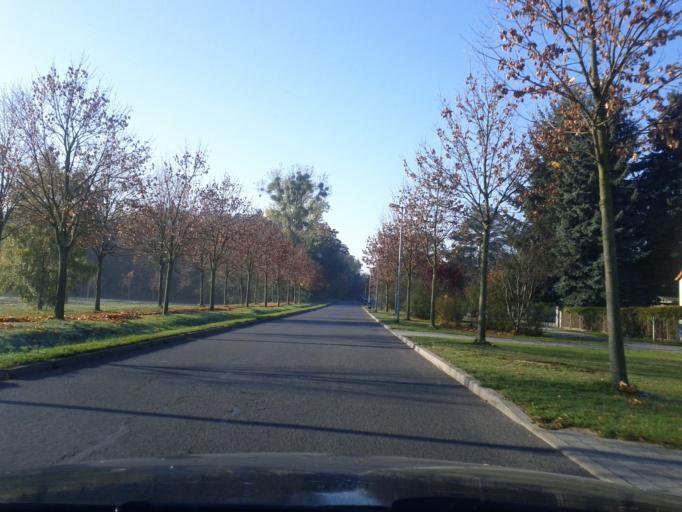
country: DE
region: Brandenburg
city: Schoneiche
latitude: 52.4673
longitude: 13.7294
